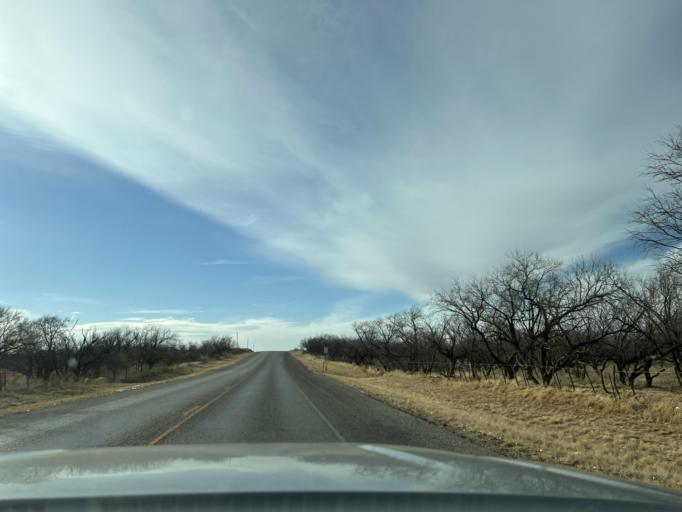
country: US
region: Texas
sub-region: Fisher County
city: Rotan
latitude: 32.7396
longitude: -100.5233
